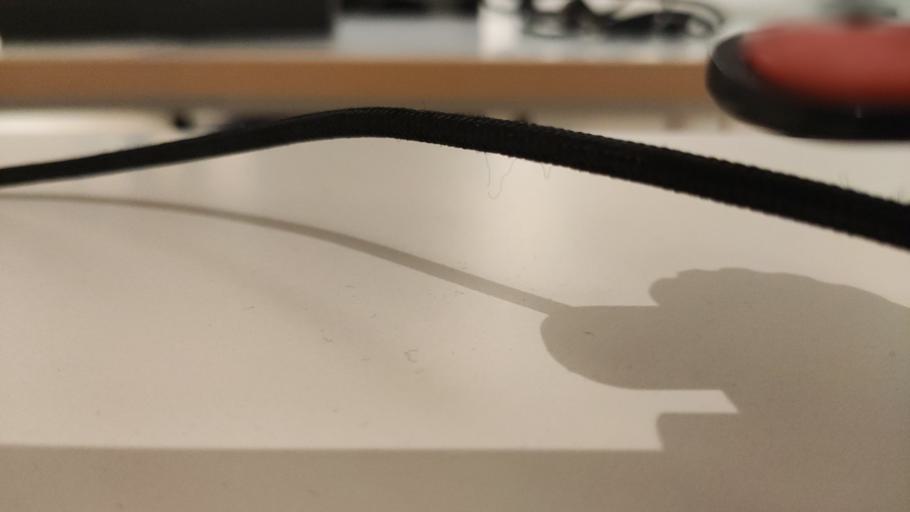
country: RU
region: Moskovskaya
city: Dorokhovo
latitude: 55.5151
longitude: 36.3505
